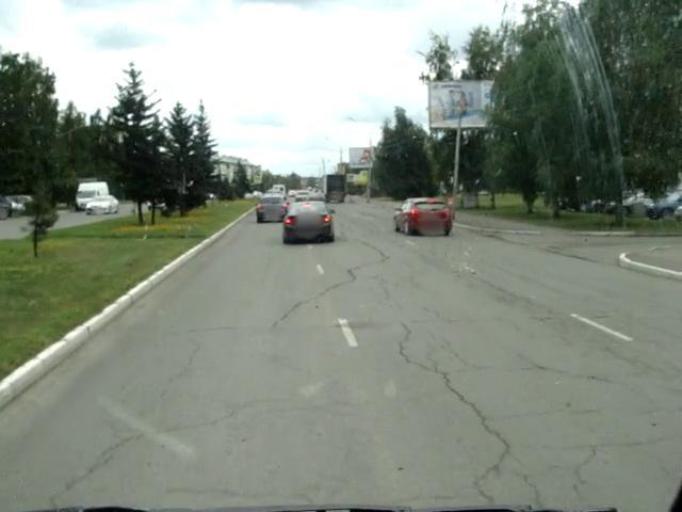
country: RU
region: Altai Krai
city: Biysk
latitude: 52.5453
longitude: 85.2151
